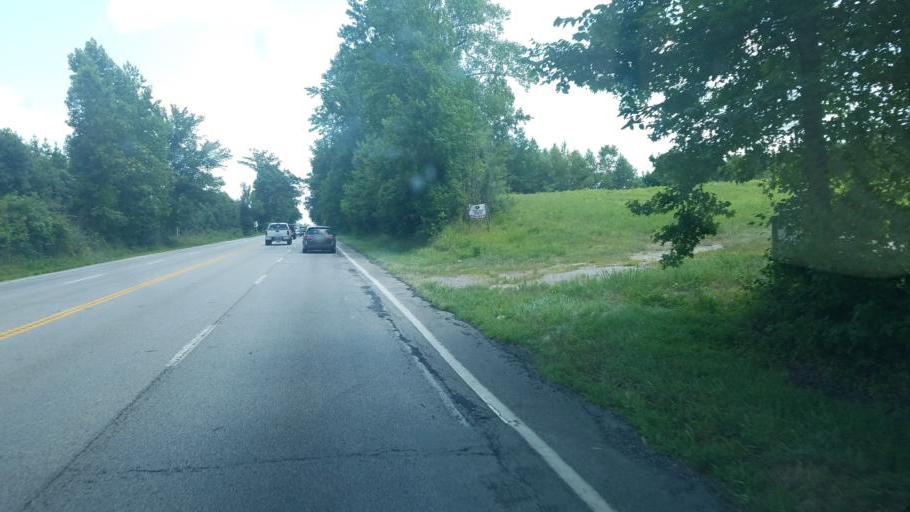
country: US
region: Virginia
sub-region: Prince George County
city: Prince George
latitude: 37.1472
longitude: -77.2619
